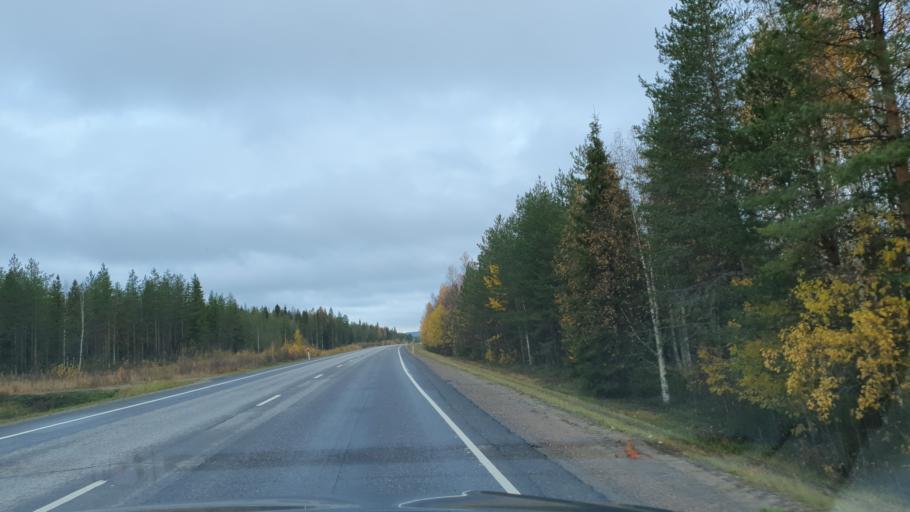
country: FI
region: Lapland
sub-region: Rovaniemi
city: Rovaniemi
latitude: 66.5515
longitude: 25.6528
